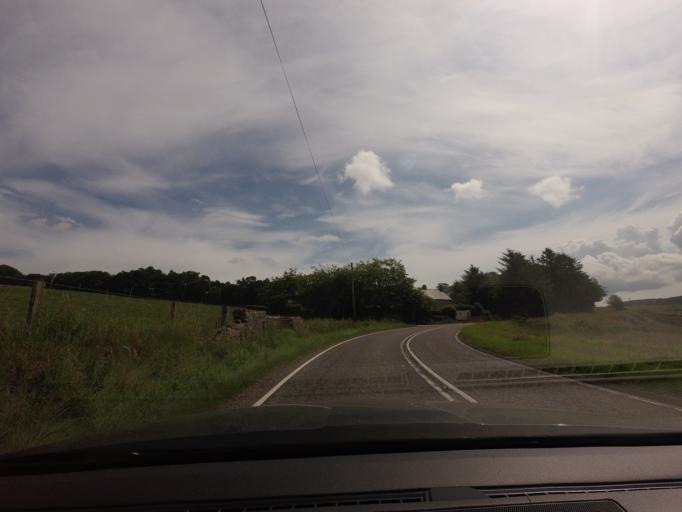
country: GB
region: Scotland
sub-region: Aberdeenshire
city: Mintlaw
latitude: 57.5299
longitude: -2.0703
